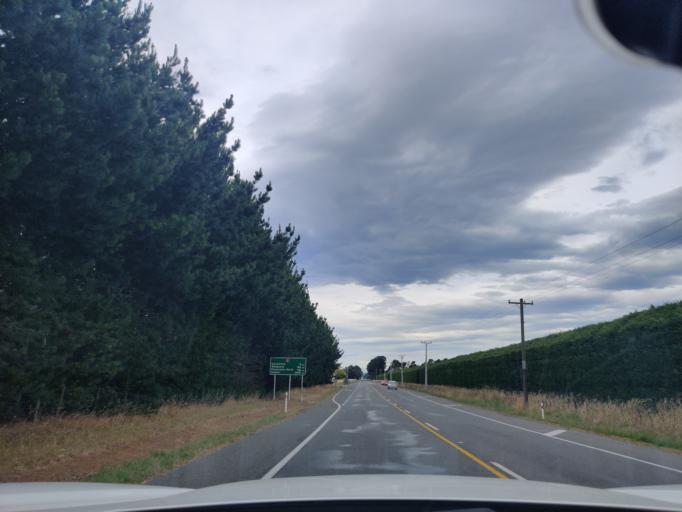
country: NZ
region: Wellington
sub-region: Masterton District
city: Masterton
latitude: -40.9892
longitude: 175.5728
